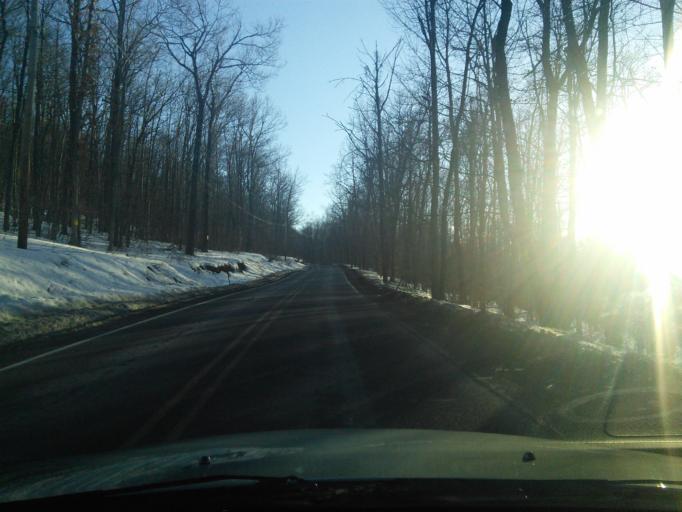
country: US
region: Pennsylvania
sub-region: Centre County
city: Park Forest Village
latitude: 40.8554
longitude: -77.9372
